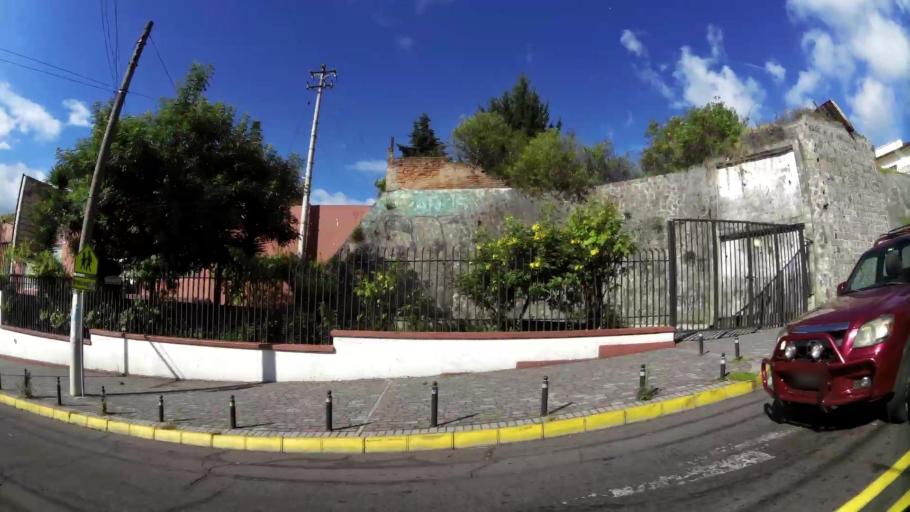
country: EC
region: Pichincha
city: Quito
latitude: -0.2159
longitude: -78.4999
